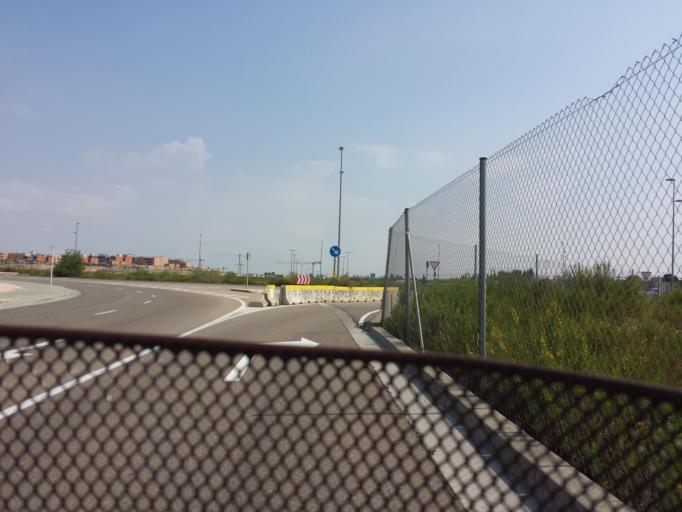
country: ES
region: Aragon
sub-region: Provincia de Zaragoza
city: Montecanal
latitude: 41.6301
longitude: -0.9529
